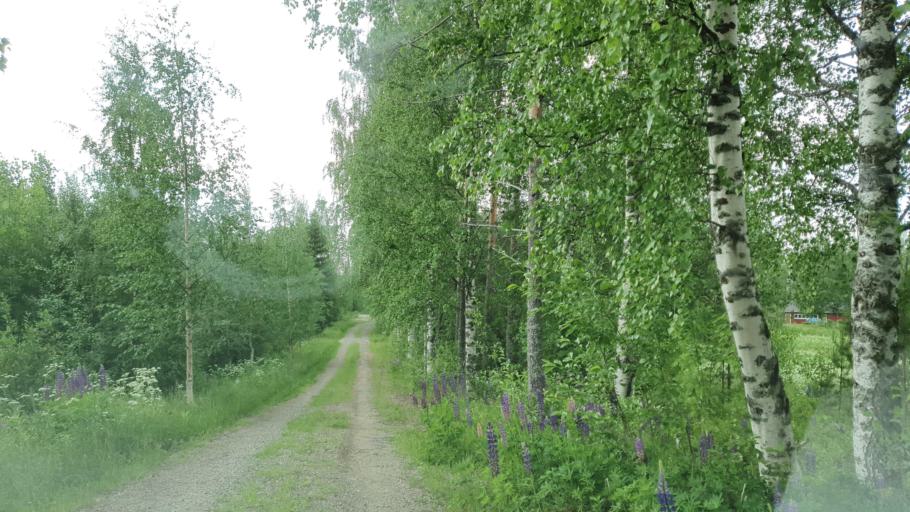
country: FI
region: Kainuu
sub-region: Kehys-Kainuu
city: Kuhmo
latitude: 64.3179
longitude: 29.8829
